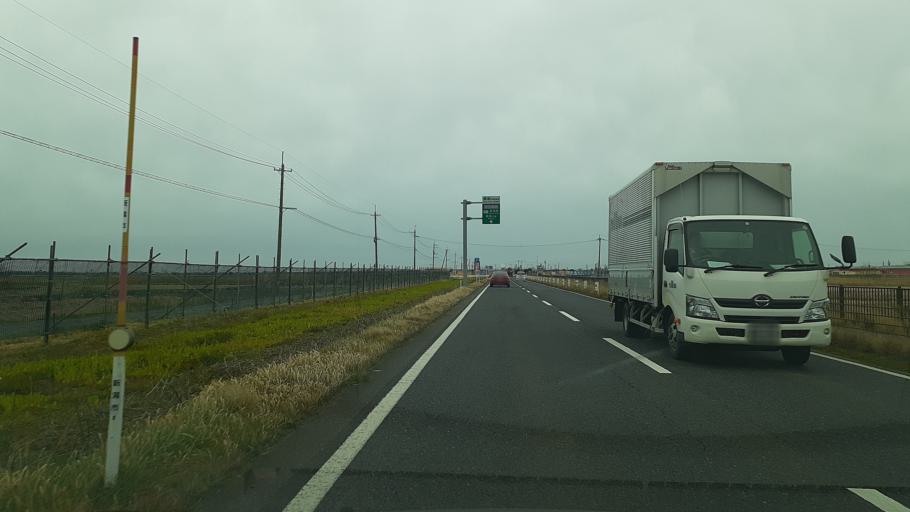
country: JP
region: Niigata
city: Niitsu-honcho
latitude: 37.8090
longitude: 139.1012
